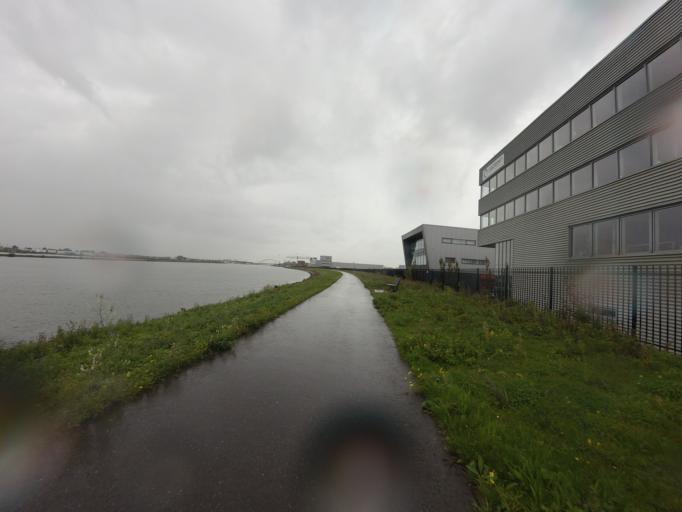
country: NL
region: South Holland
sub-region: Gemeente Papendrecht
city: Papendrecht
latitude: 51.8404
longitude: 4.6737
